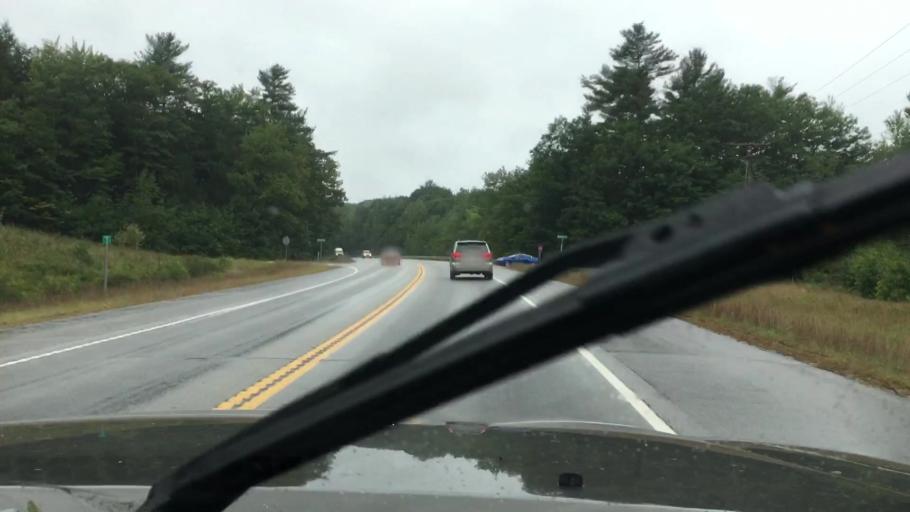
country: US
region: New Hampshire
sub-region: Cheshire County
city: Keene
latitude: 42.9306
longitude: -72.3289
